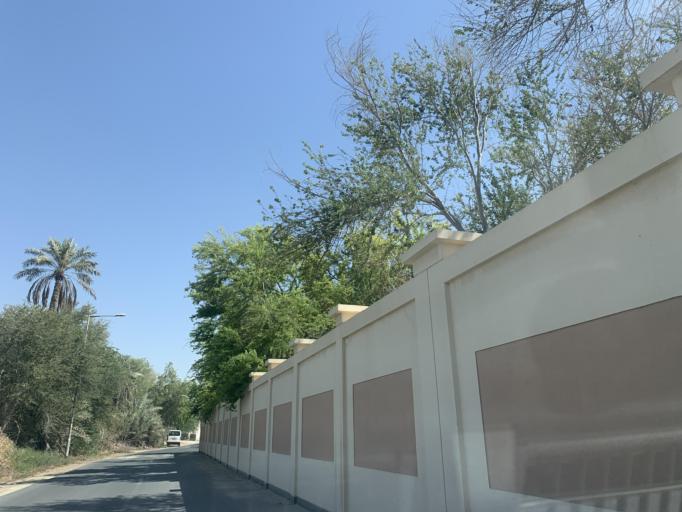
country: BH
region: Manama
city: Jidd Hafs
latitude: 26.2261
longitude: 50.4990
